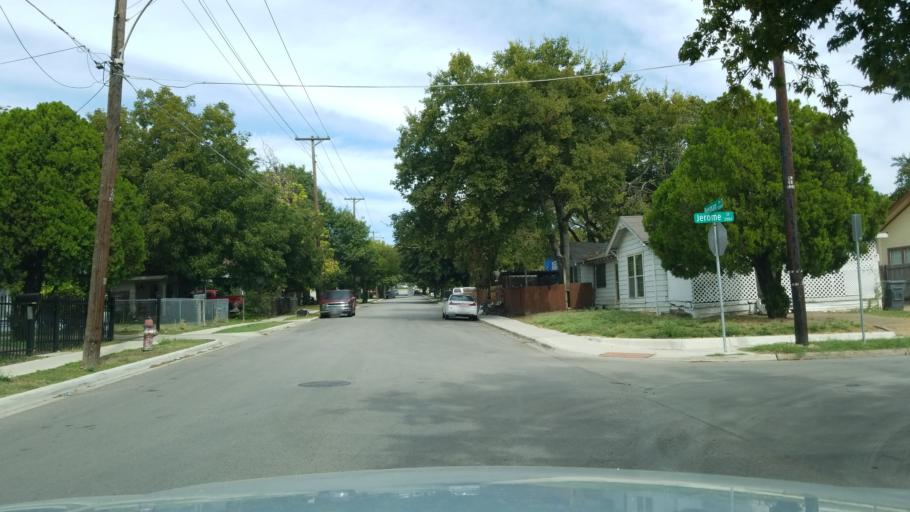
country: US
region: Texas
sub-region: Dallas County
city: Dallas
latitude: 32.7872
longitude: -96.7444
